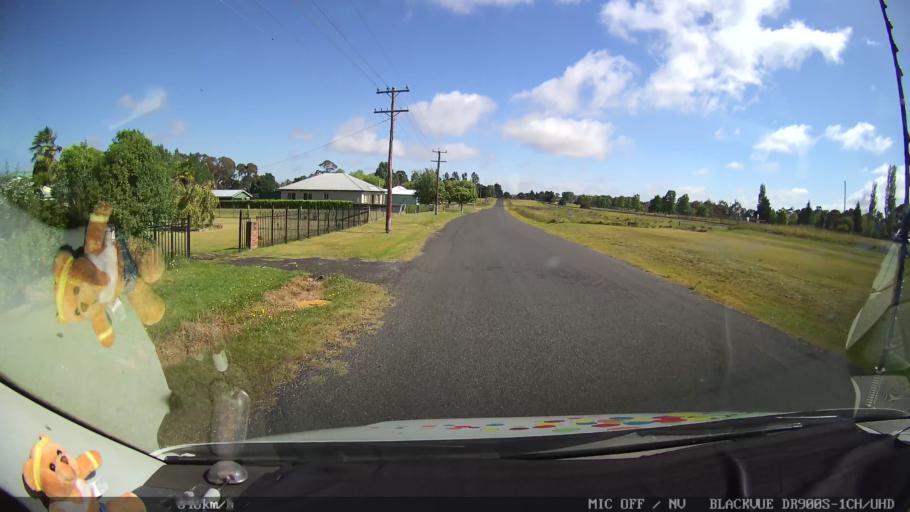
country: AU
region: New South Wales
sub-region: Guyra
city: Guyra
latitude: -30.2117
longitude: 151.6733
